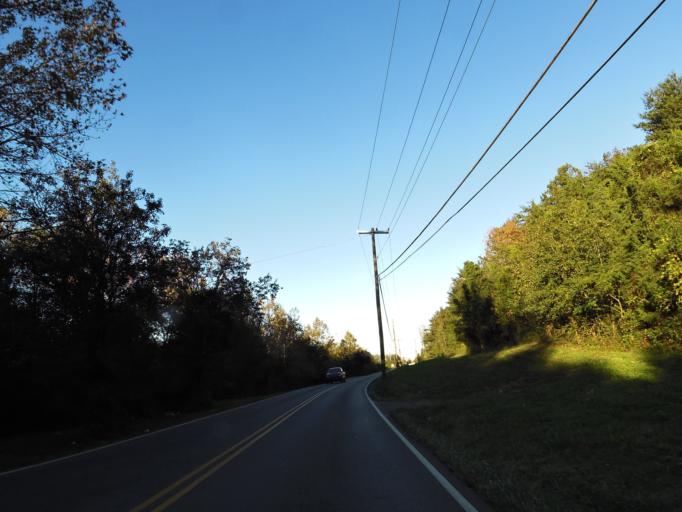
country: US
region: Tennessee
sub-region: Knox County
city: Knoxville
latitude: 35.9988
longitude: -84.0301
